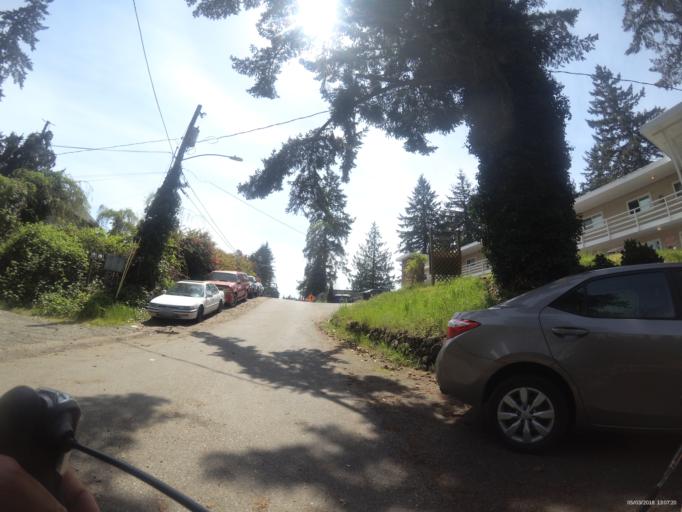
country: US
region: Washington
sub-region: Pierce County
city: McChord Air Force Base
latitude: 47.1439
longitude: -122.5019
